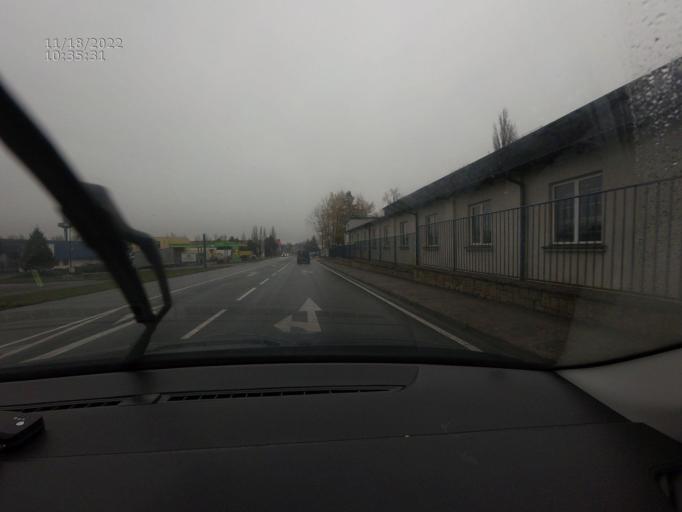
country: CZ
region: Central Bohemia
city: Zebrak
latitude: 49.8693
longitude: 13.8953
